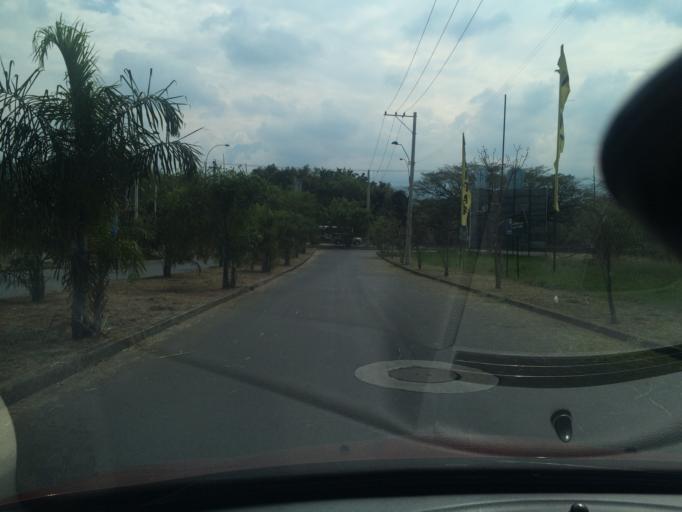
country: CO
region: Valle del Cauca
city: Cali
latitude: 3.3564
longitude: -76.5228
